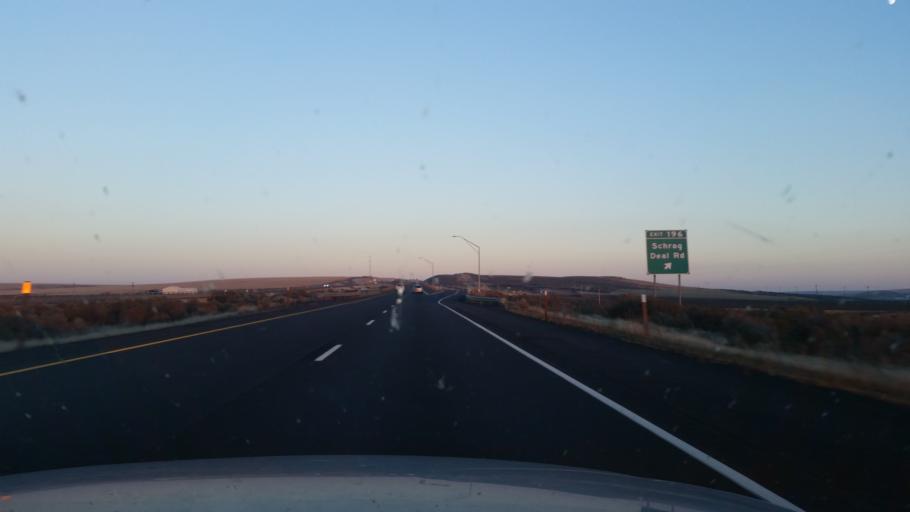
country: US
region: Washington
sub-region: Grant County
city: Warden
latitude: 47.0871
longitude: -118.8823
